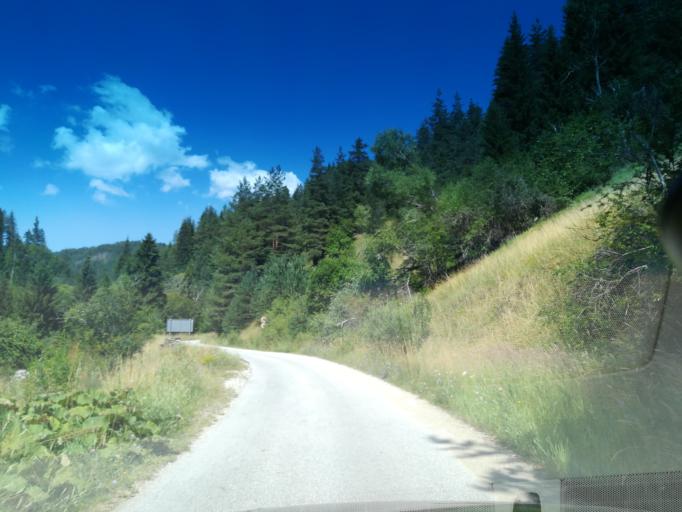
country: BG
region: Smolyan
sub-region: Obshtina Smolyan
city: Smolyan
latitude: 41.6599
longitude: 24.8155
